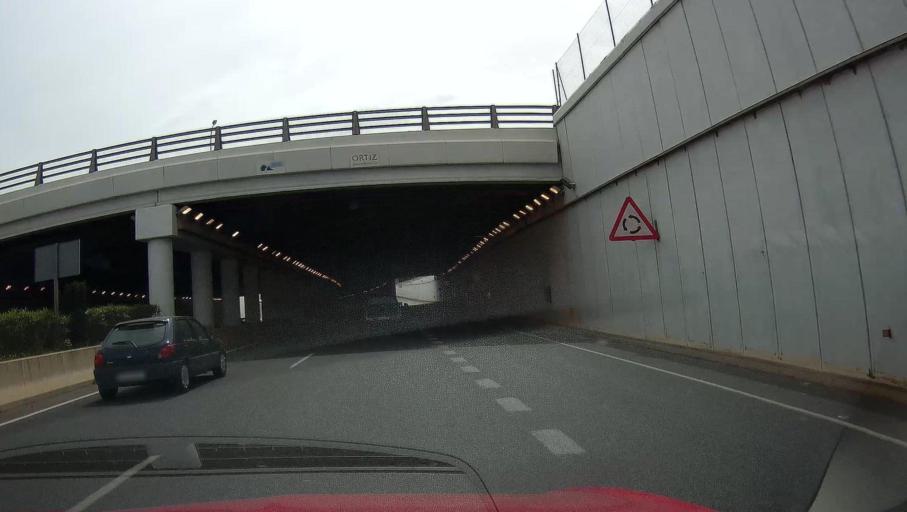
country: ES
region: Balearic Islands
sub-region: Illes Balears
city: Ibiza
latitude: 38.8974
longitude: 1.4020
